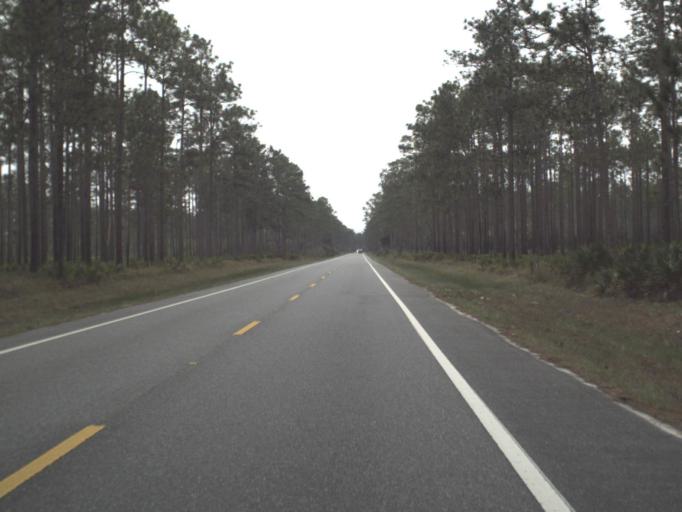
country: US
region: Florida
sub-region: Gulf County
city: Wewahitchka
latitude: 29.9859
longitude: -84.9760
